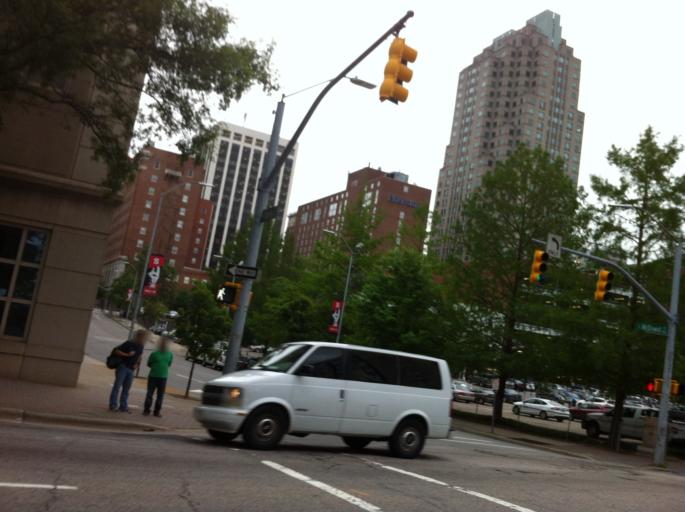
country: US
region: North Carolina
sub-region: Wake County
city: Raleigh
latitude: 35.7759
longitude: -78.6420
